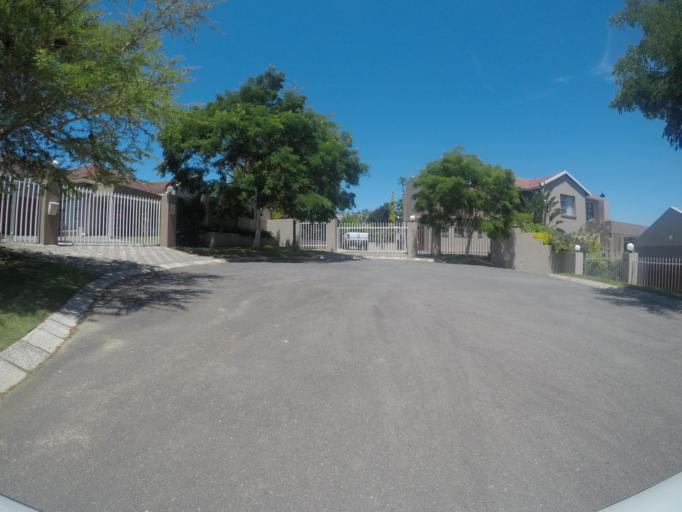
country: ZA
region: Eastern Cape
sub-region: Buffalo City Metropolitan Municipality
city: East London
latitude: -32.9276
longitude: 27.9982
